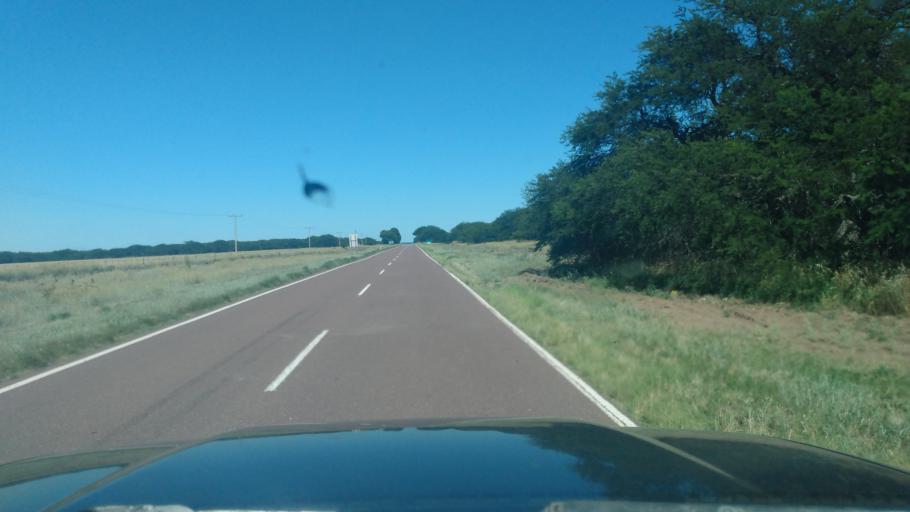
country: AR
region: La Pampa
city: General Acha
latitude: -37.4170
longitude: -64.8490
